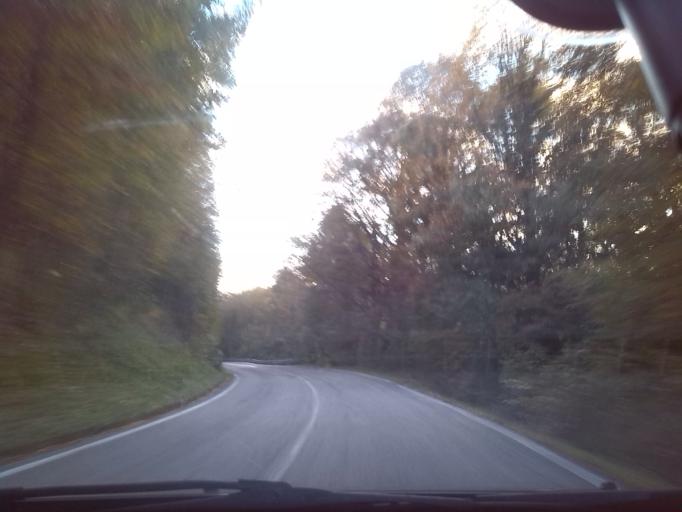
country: IT
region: Friuli Venezia Giulia
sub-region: Provincia di Udine
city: Savogna
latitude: 46.1833
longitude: 13.5587
